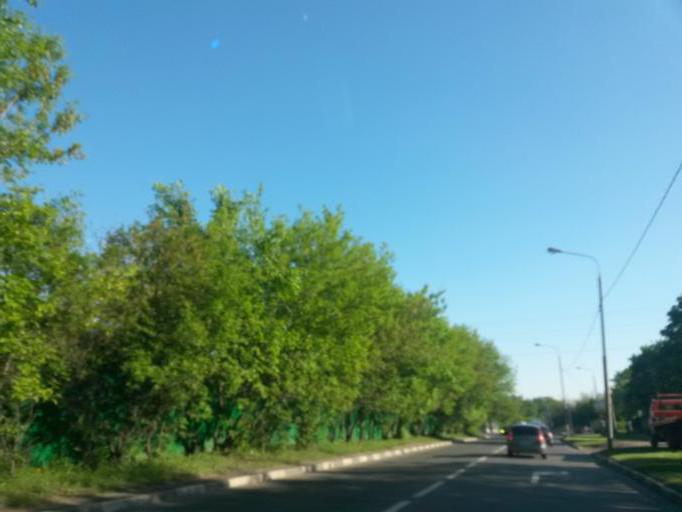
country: RU
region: Moscow
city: Orekhovo-Borisovo Severnoye
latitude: 55.6338
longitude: 37.6852
